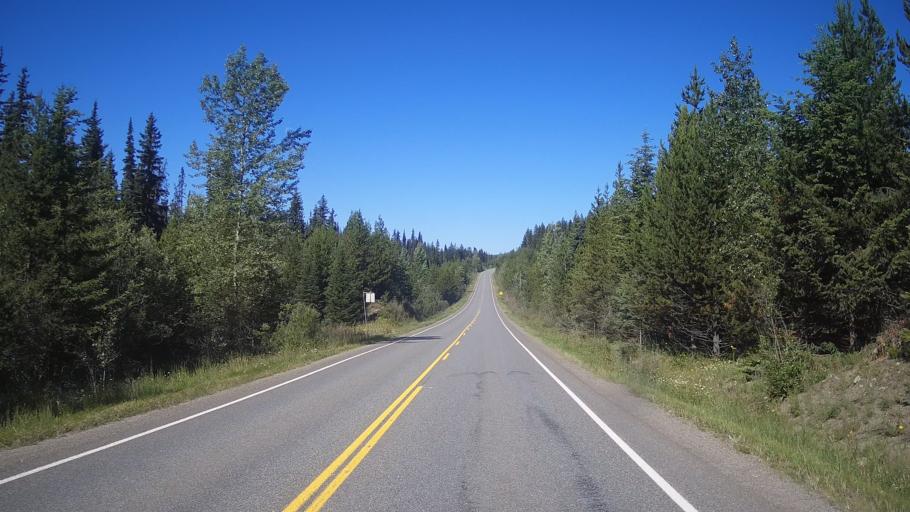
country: CA
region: British Columbia
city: Kamloops
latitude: 51.4970
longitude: -120.3809
